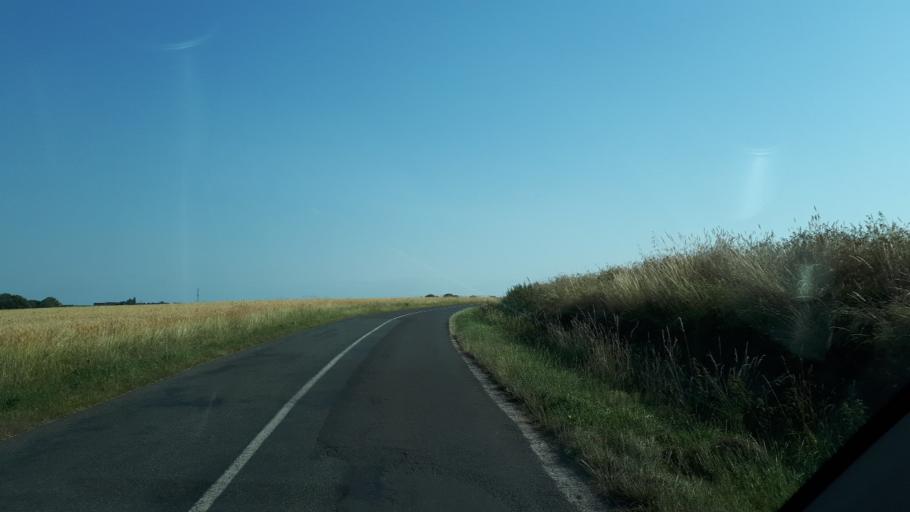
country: FR
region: Centre
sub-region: Departement du Loir-et-Cher
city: La Ville-aux-Clercs
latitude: 47.9065
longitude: 1.0453
